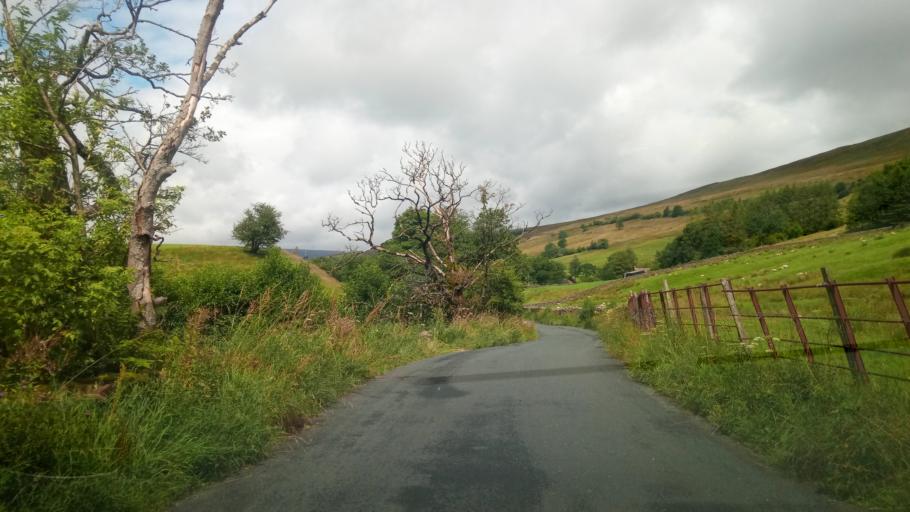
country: GB
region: England
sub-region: North Yorkshire
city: Ingleton
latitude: 54.2650
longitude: -2.3507
